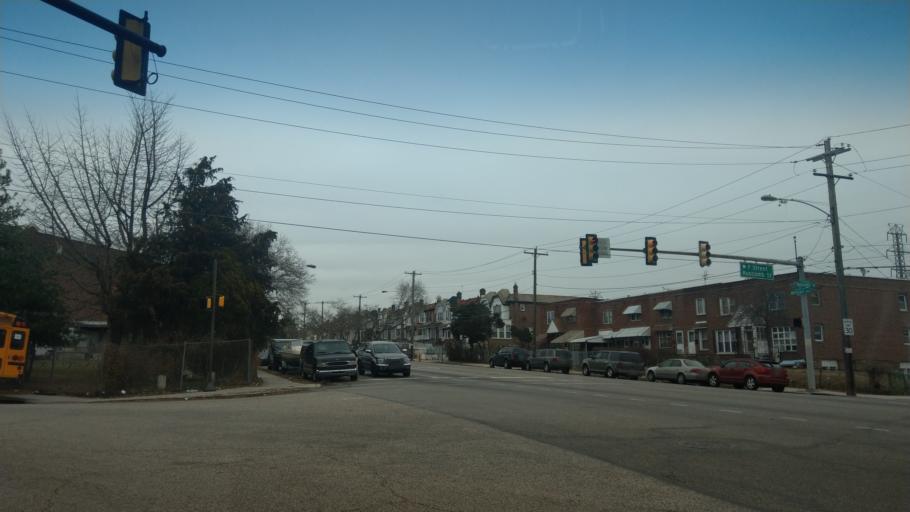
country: US
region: Pennsylvania
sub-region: Montgomery County
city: Rockledge
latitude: 40.0248
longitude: -75.1099
